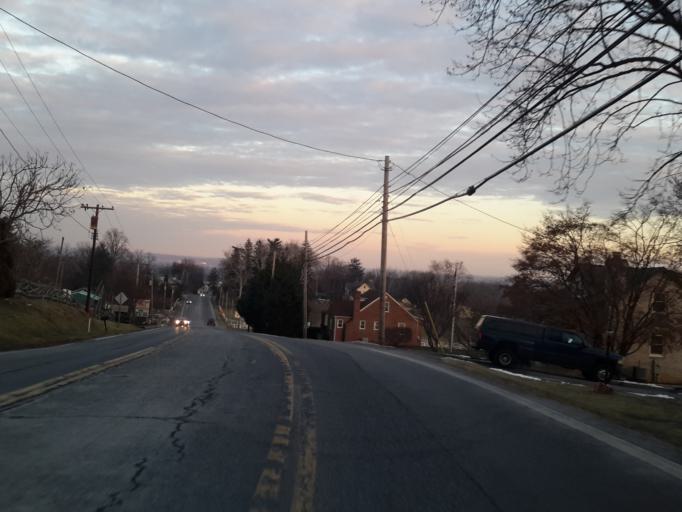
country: US
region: Maryland
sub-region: Frederick County
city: Braddock Heights
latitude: 39.4208
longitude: -77.4797
